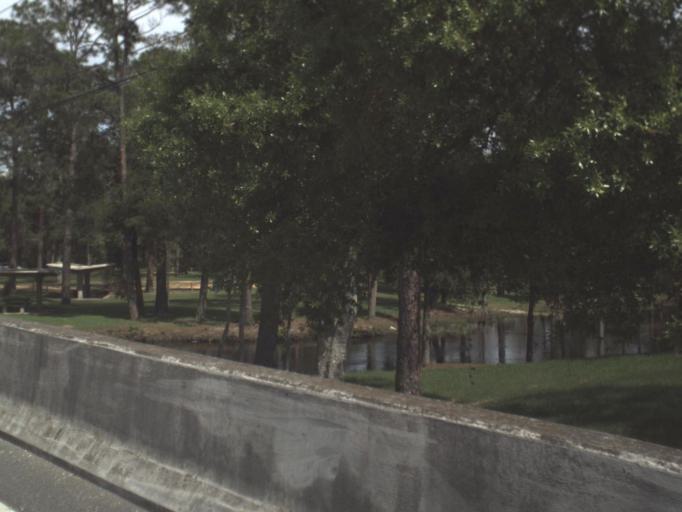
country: US
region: Florida
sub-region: Santa Rosa County
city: Bagdad
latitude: 30.6072
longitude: -87.0623
